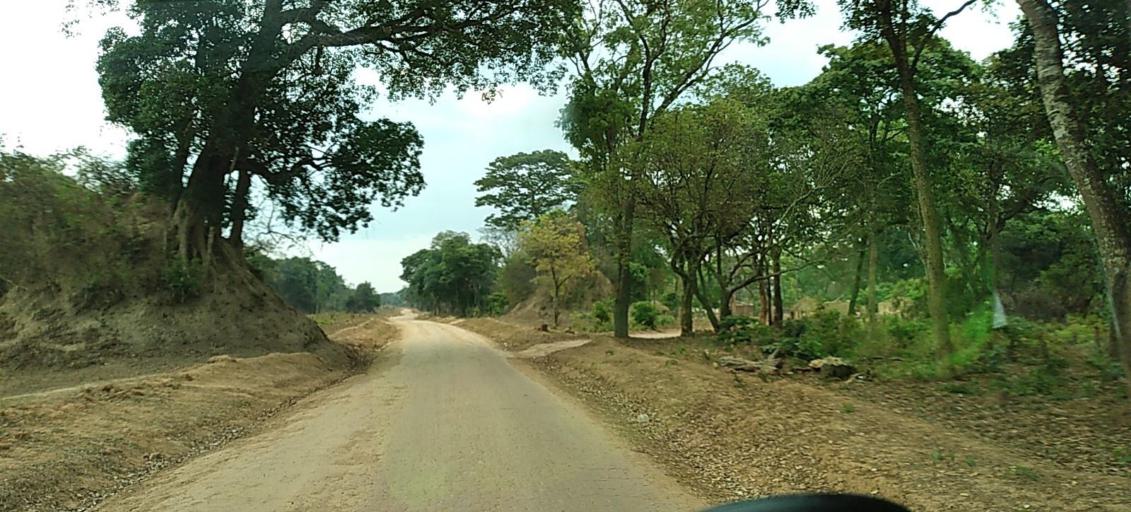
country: ZM
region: North-Western
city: Solwezi
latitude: -12.7849
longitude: 26.5117
